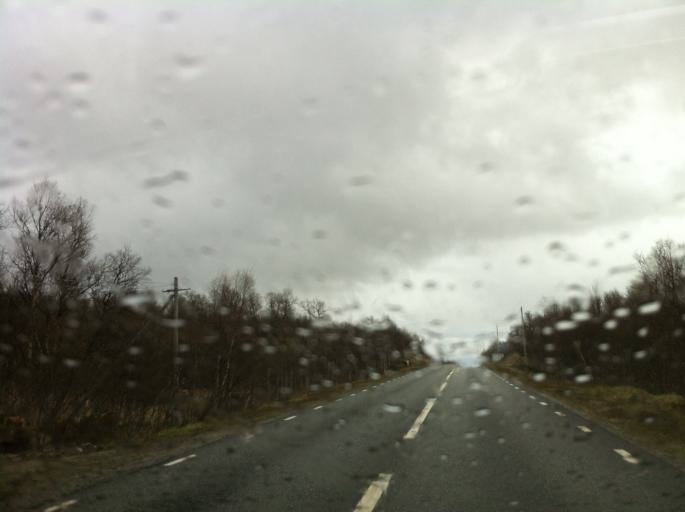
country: NO
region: Sor-Trondelag
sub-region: Tydal
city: Aas
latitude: 62.6217
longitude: 12.1312
